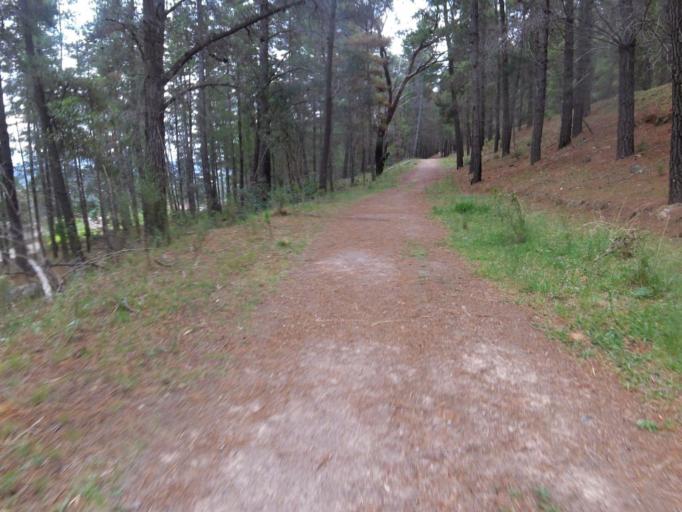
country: AU
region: Australian Capital Territory
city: Macarthur
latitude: -35.3661
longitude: 149.1147
